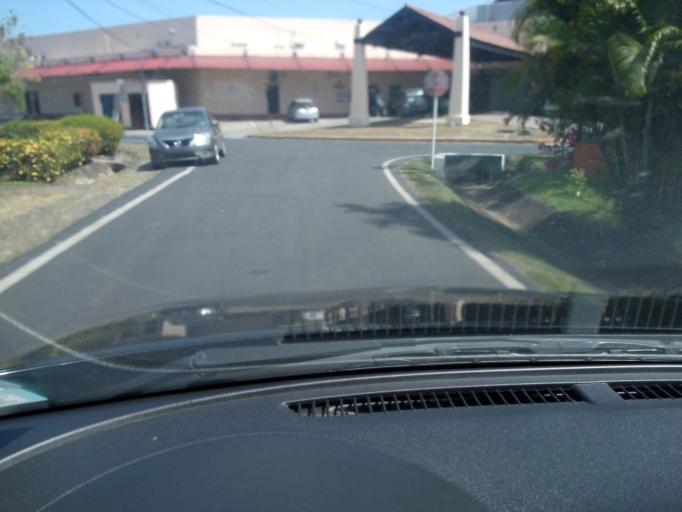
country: PA
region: Veraguas
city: Santiago de Veraguas
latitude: 8.1056
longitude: -80.9716
